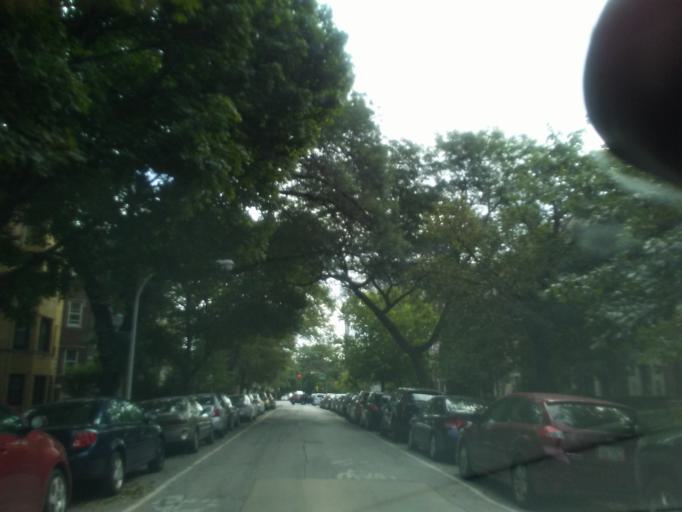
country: US
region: Illinois
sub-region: Cook County
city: Evanston
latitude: 42.0025
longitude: -87.6626
